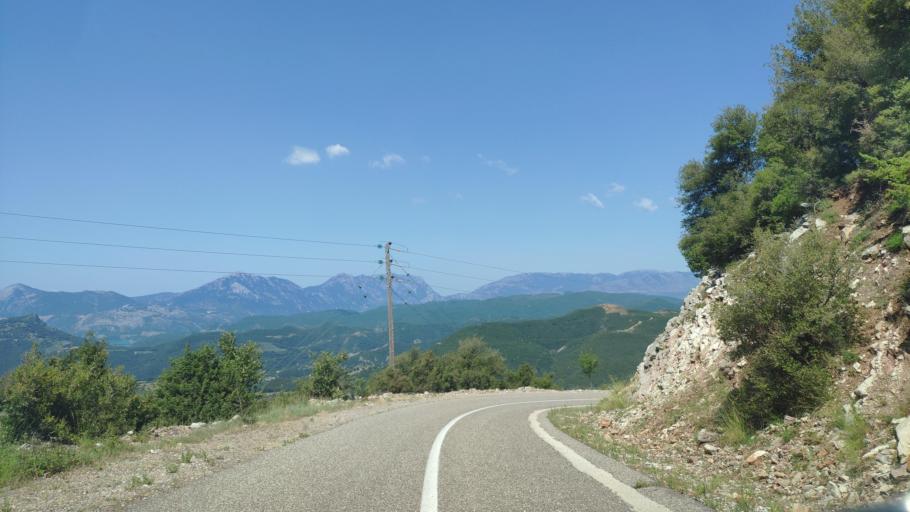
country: GR
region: Central Greece
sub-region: Nomos Evrytanias
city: Kerasochori
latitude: 39.0067
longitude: 21.5951
